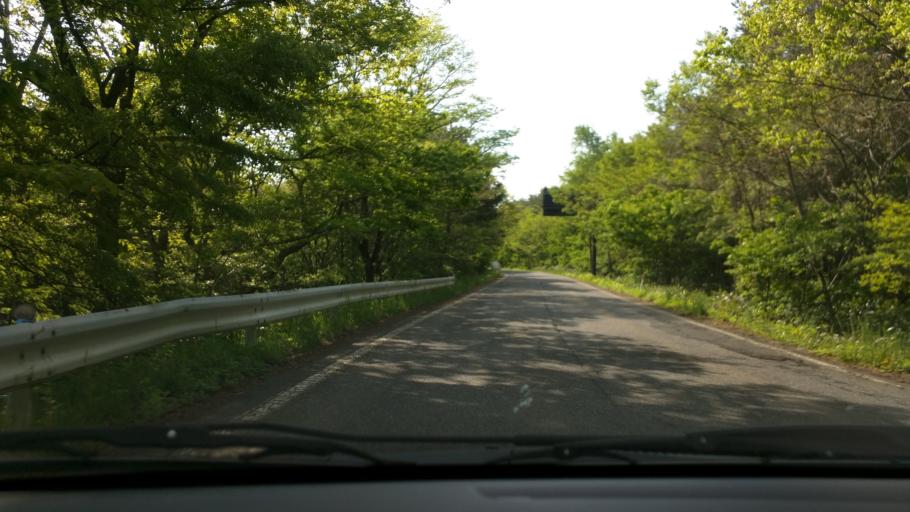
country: JP
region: Tochigi
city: Kuroiso
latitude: 37.2402
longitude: 140.0673
